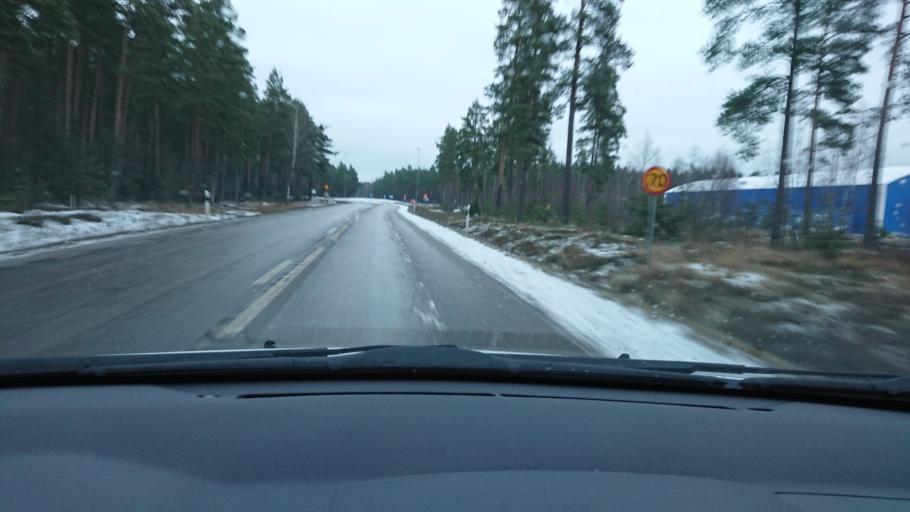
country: SE
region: Kalmar
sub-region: Hultsfreds Kommun
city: Hultsfred
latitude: 57.5091
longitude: 15.8338
